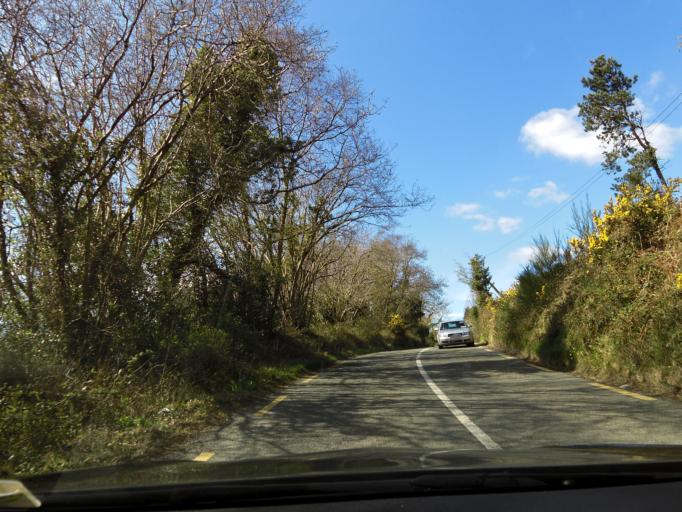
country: IE
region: Leinster
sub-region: Wicklow
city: Aughrim
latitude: 52.8487
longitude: -6.2811
